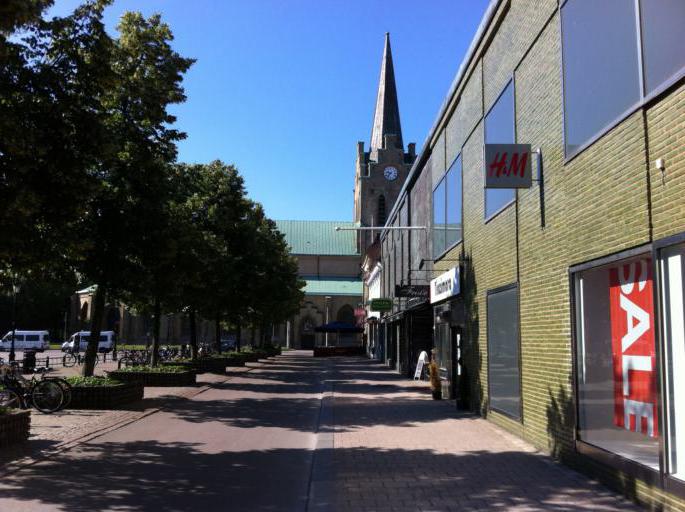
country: SE
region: Halland
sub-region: Halmstads Kommun
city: Halmstad
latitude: 56.6744
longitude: 12.8567
